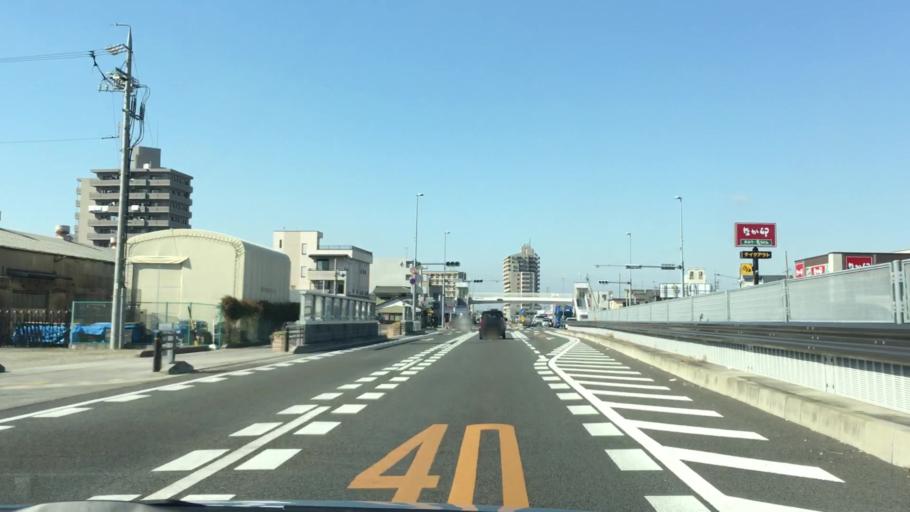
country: JP
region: Aichi
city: Okazaki
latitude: 34.9616
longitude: 137.1433
